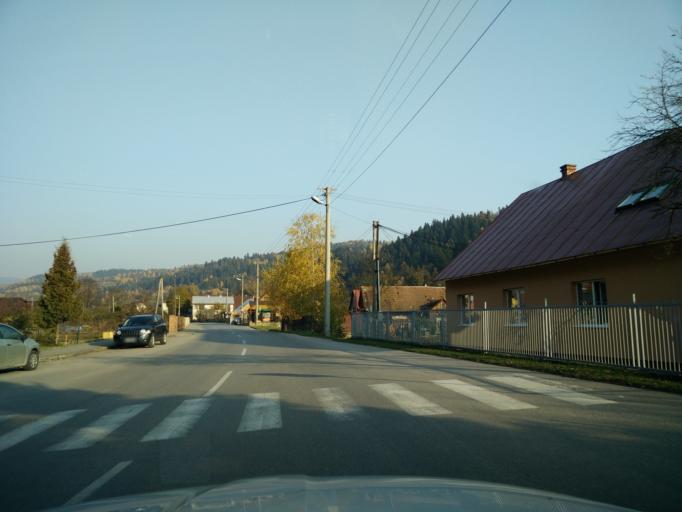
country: SK
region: Zilinsky
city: Cadca
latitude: 49.4208
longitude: 18.8529
